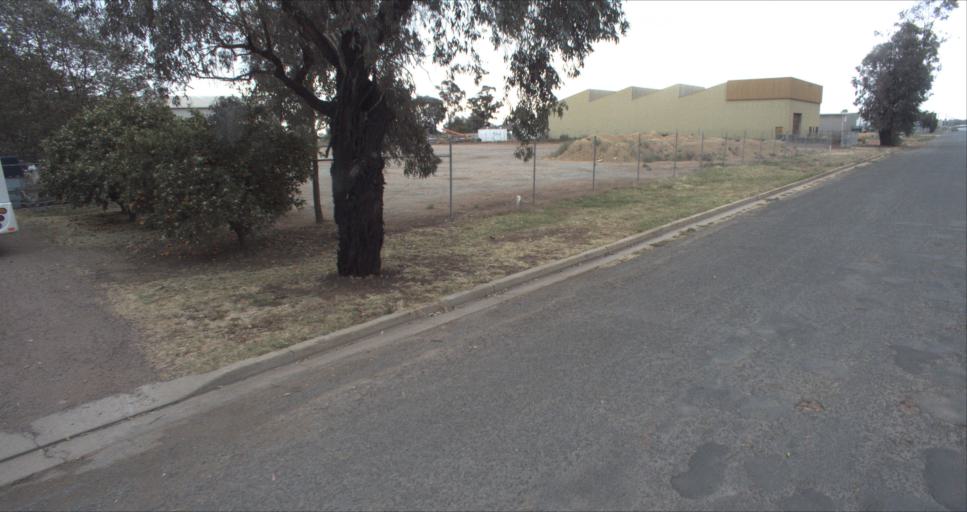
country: AU
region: New South Wales
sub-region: Leeton
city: Leeton
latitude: -34.5501
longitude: 146.3870
